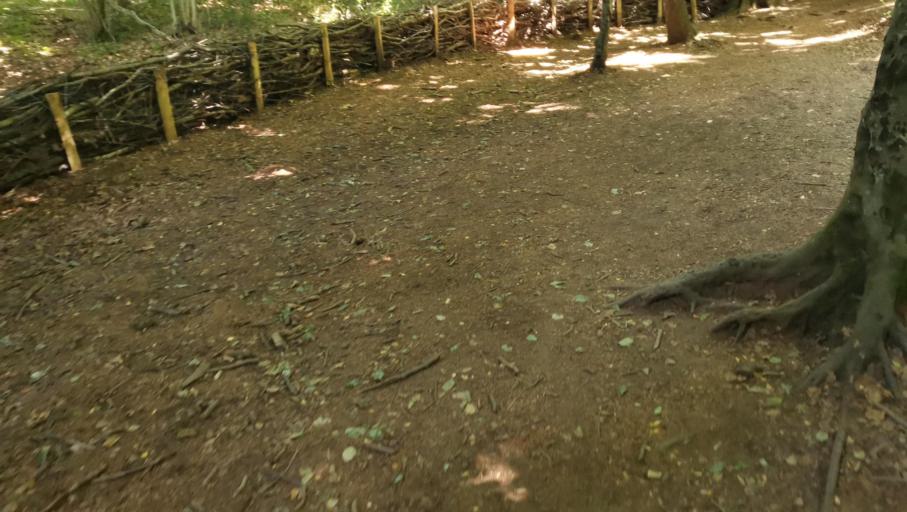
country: FR
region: Auvergne
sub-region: Departement du Puy-de-Dome
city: Orcines
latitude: 45.8000
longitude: 2.9773
